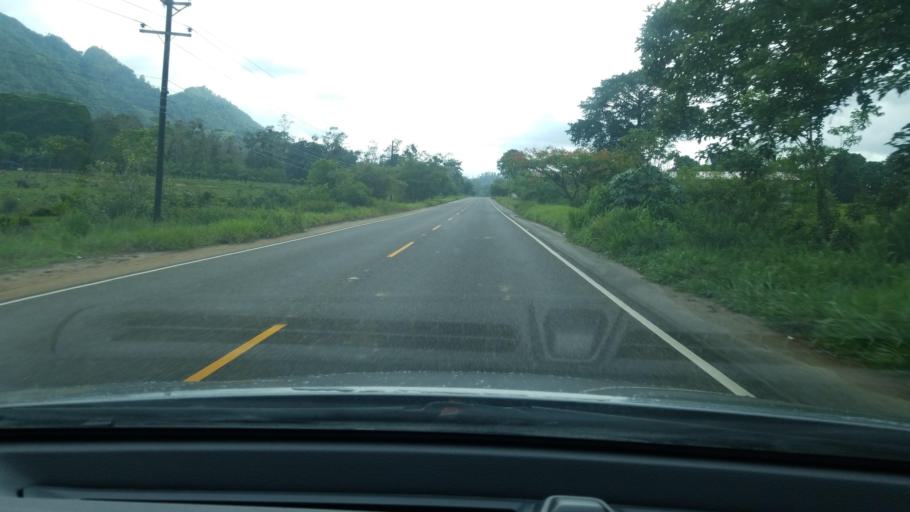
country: HN
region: Cortes
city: Rio Chiquito
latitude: 15.6172
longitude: -88.2737
